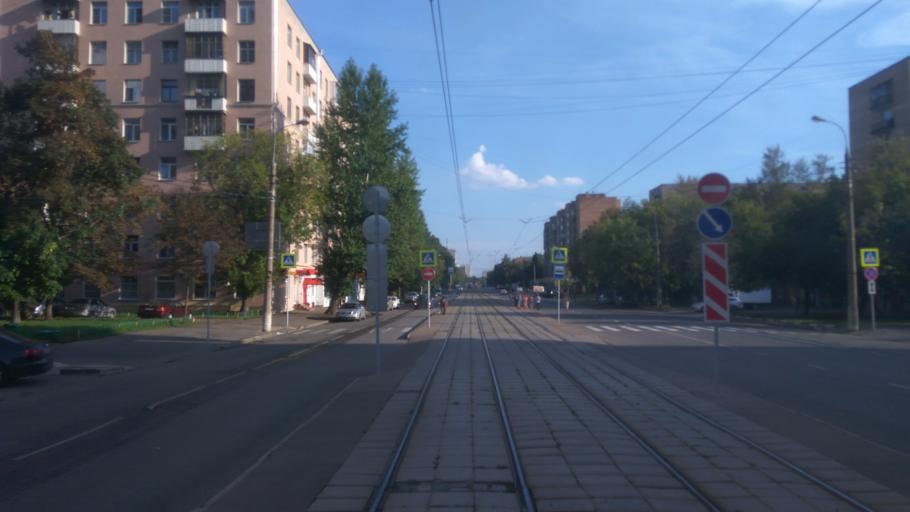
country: RU
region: Moskovskaya
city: Izmaylovo
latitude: 55.7639
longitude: 37.7847
